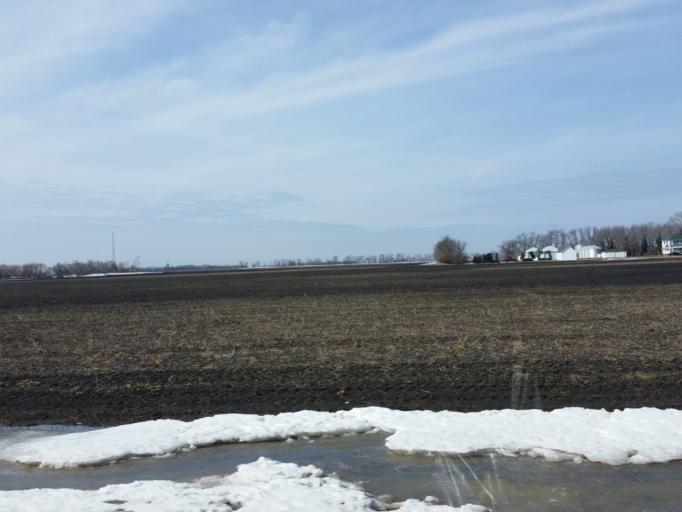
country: US
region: North Dakota
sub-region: Walsh County
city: Grafton
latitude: 48.3057
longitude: -97.2111
